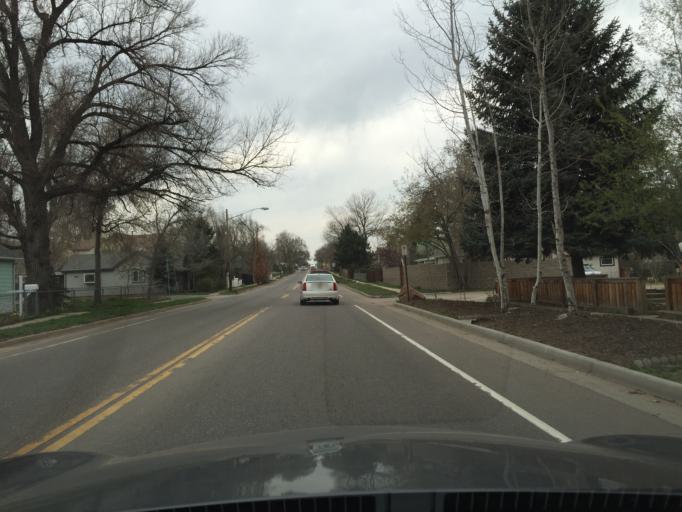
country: US
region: Colorado
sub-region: Boulder County
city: Lafayette
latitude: 40.0003
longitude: -105.0836
